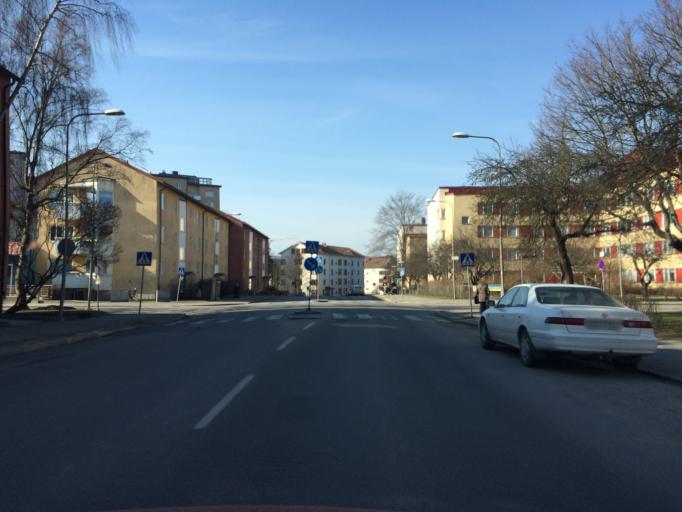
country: SE
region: Stockholm
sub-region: Stockholms Kommun
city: Arsta
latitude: 59.2997
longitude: 18.0430
